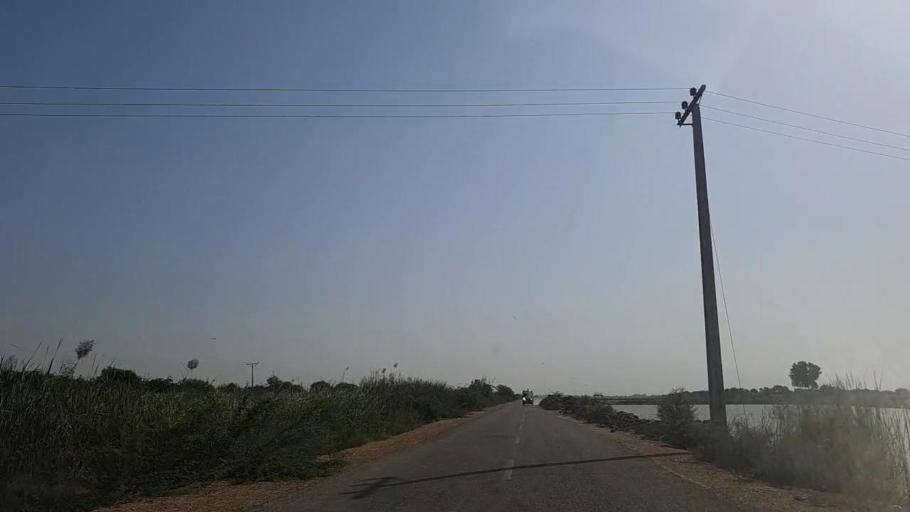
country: PK
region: Sindh
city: Jati
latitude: 24.5104
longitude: 68.2745
